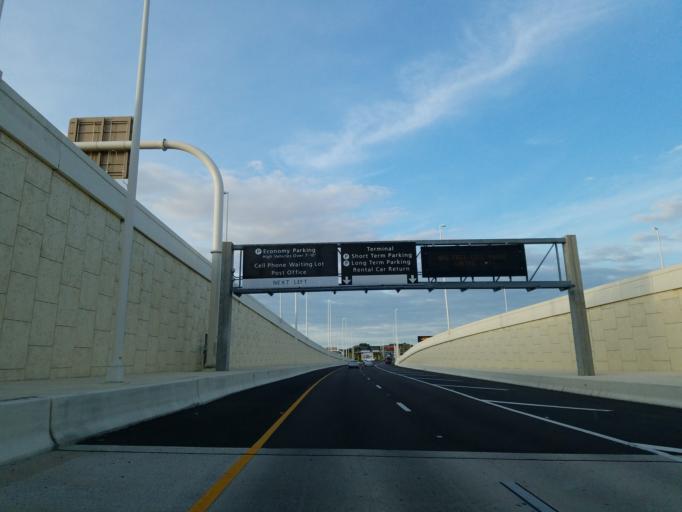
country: US
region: Florida
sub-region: Hillsborough County
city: Town 'n' Country
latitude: 27.9608
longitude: -82.5389
